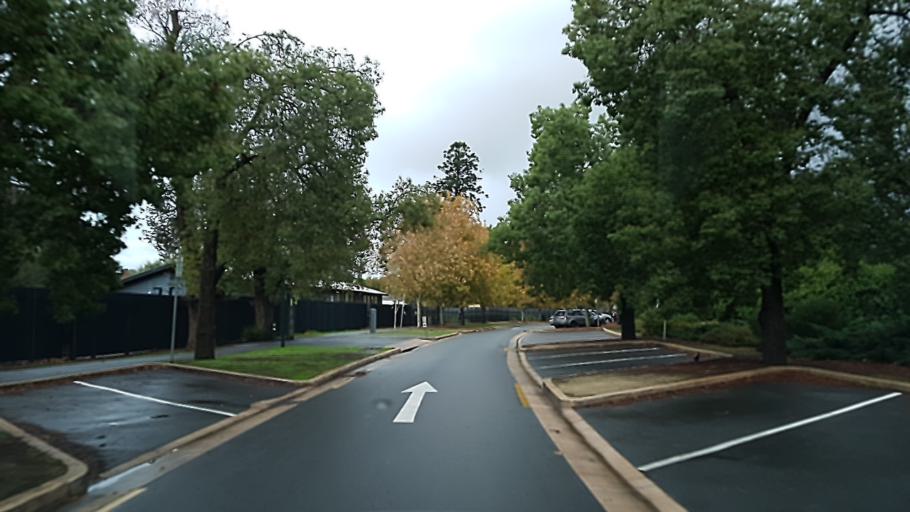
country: AU
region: South Australia
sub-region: Adelaide
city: Adelaide
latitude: -34.9140
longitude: 138.6074
